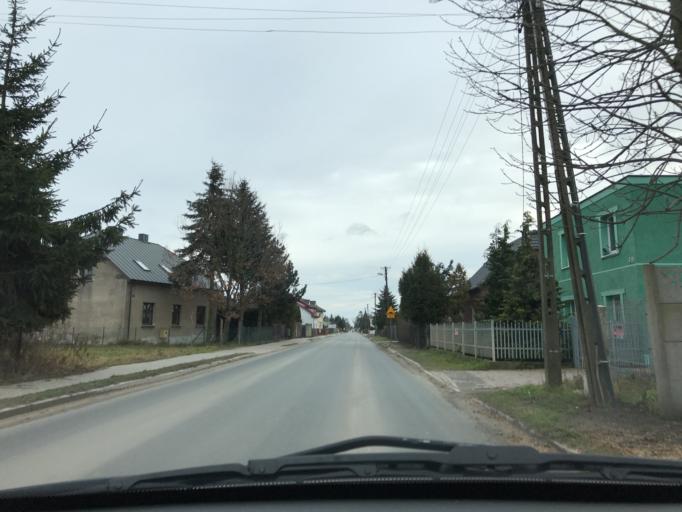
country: PL
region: Greater Poland Voivodeship
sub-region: Powiat poznanski
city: Baranowo
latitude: 52.4002
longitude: 16.7471
